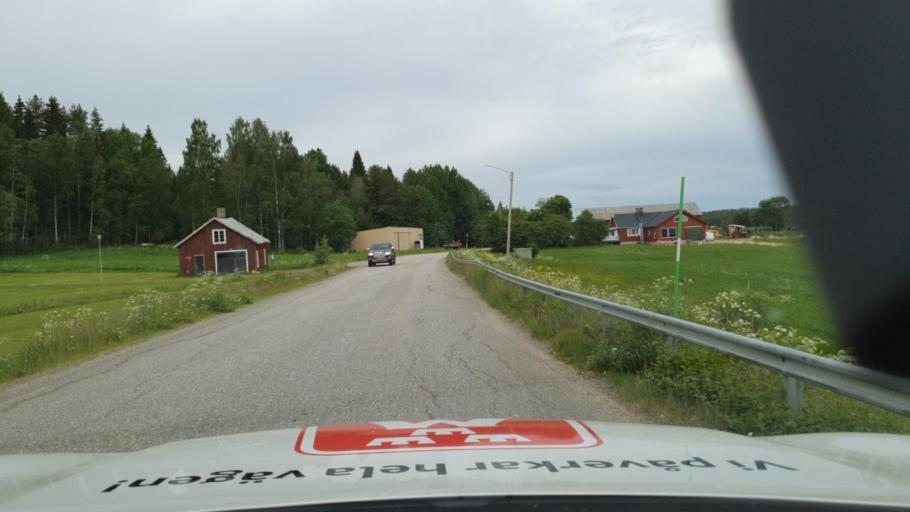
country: SE
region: Vaesterbotten
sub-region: Robertsfors Kommun
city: Robertsfors
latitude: 64.2512
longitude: 20.6581
